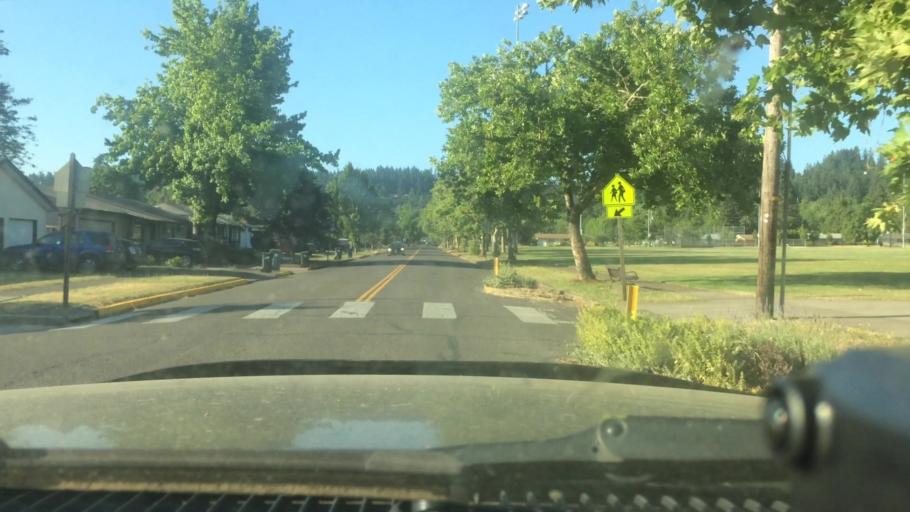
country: US
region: Oregon
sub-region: Lane County
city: Eugene
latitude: 44.0356
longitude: -123.1123
